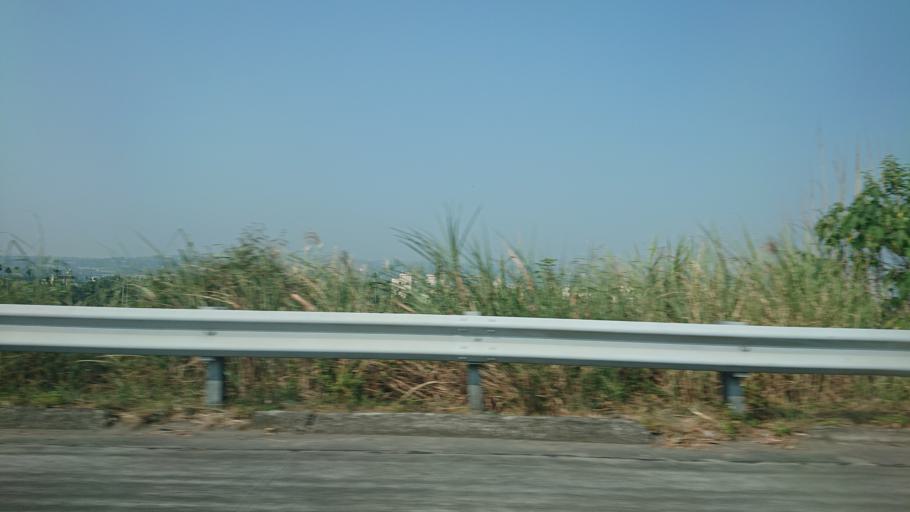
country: TW
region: Taiwan
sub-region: Nantou
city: Nantou
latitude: 23.8905
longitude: 120.7103
